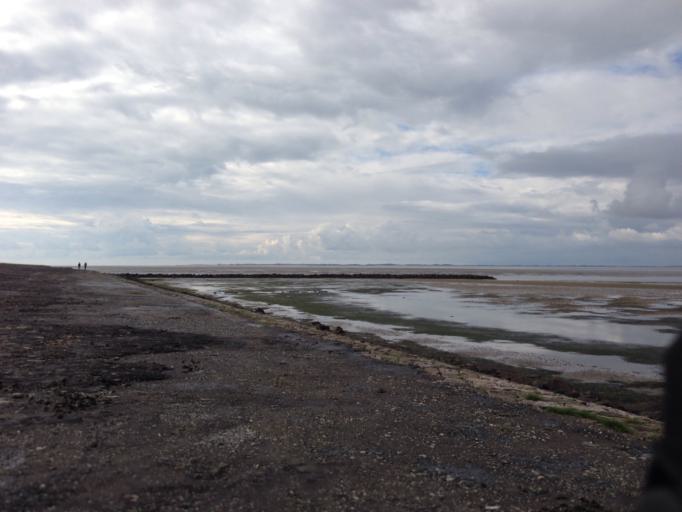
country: DE
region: Schleswig-Holstein
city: Dunsum
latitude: 54.7461
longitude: 8.4303
